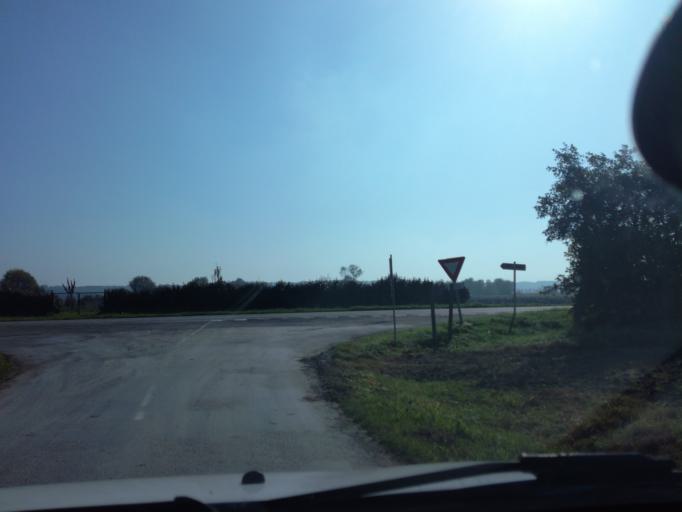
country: FR
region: Brittany
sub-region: Departement d'Ille-et-Vilaine
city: Cherrueix
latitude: 48.6004
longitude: -1.6871
